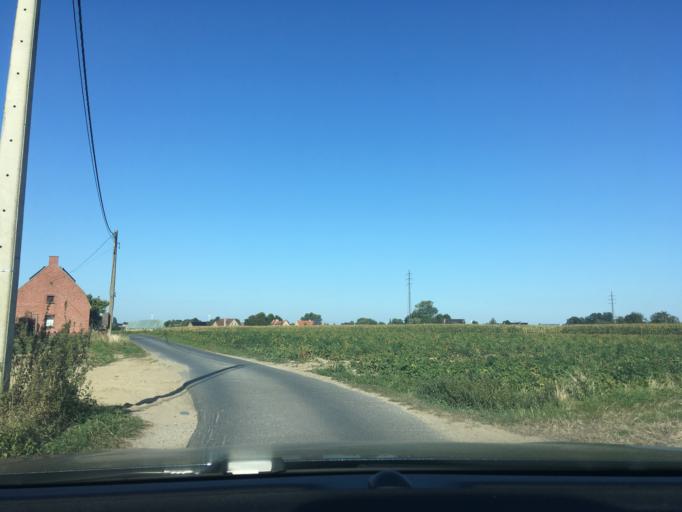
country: BE
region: Flanders
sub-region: Provincie West-Vlaanderen
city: Ledegem
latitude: 50.9024
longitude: 3.1559
